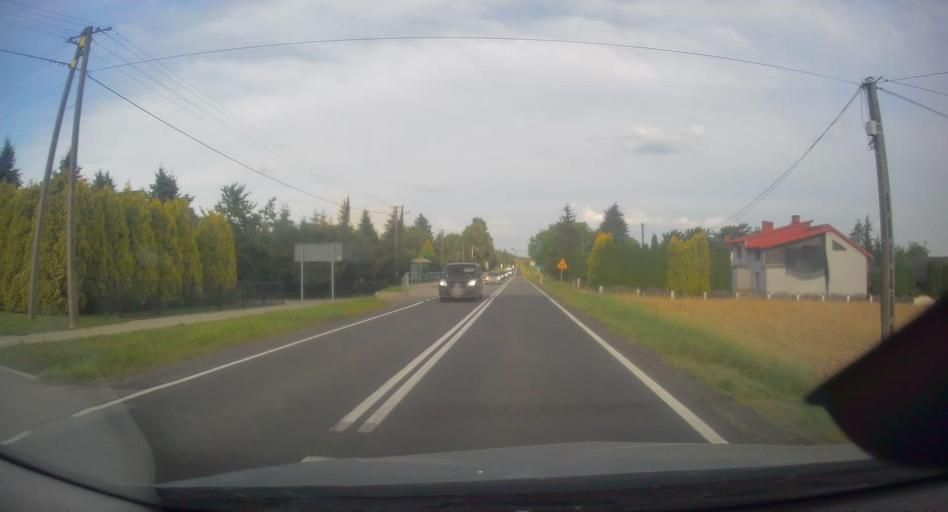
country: PL
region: Lesser Poland Voivodeship
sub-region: Powiat bochenski
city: Dziewin
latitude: 50.1438
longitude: 20.4639
